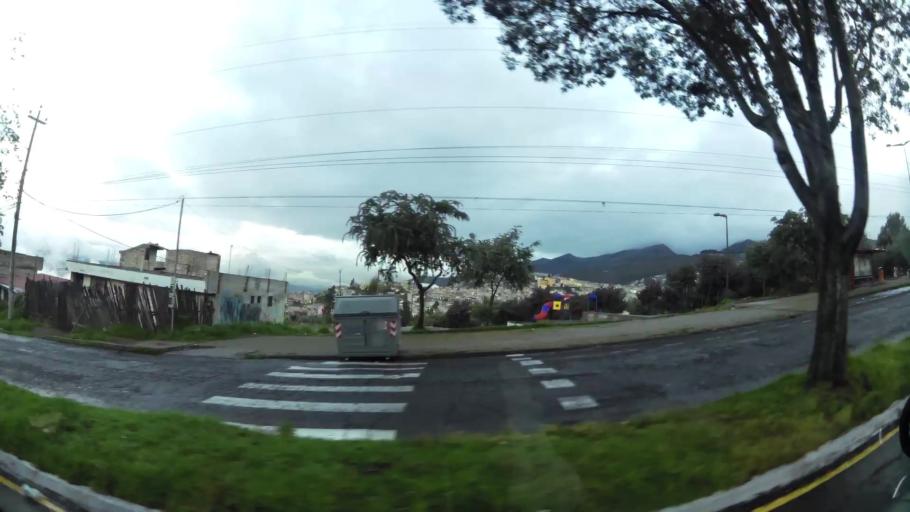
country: EC
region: Pichincha
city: Quito
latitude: -0.0902
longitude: -78.5180
